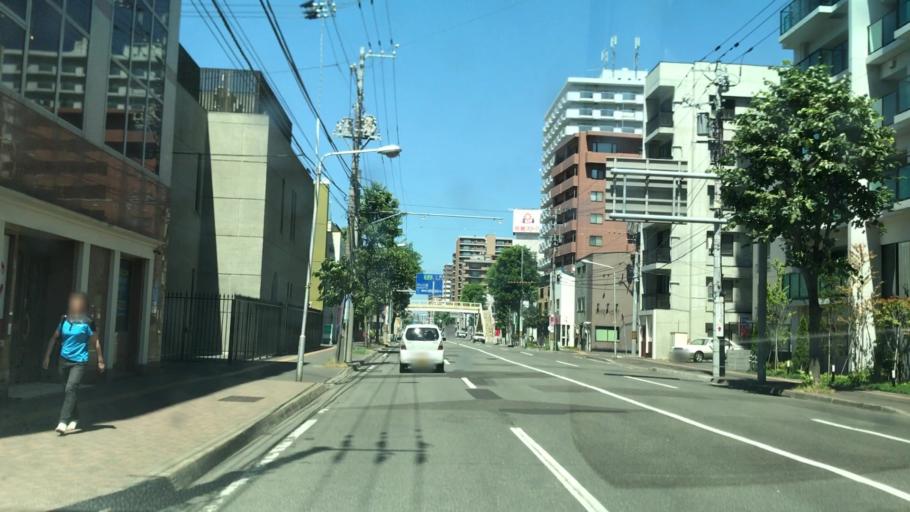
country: JP
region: Hokkaido
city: Sapporo
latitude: 43.0567
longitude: 141.3202
